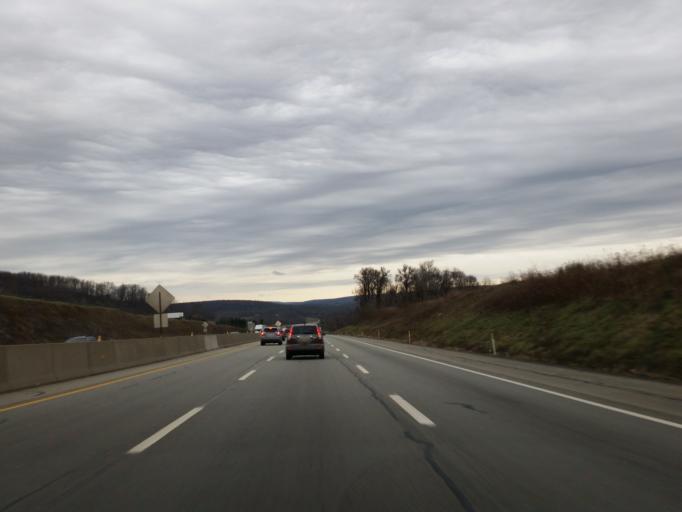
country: US
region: Pennsylvania
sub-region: Fayette County
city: Bear Rocks
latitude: 40.1135
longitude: -79.3533
